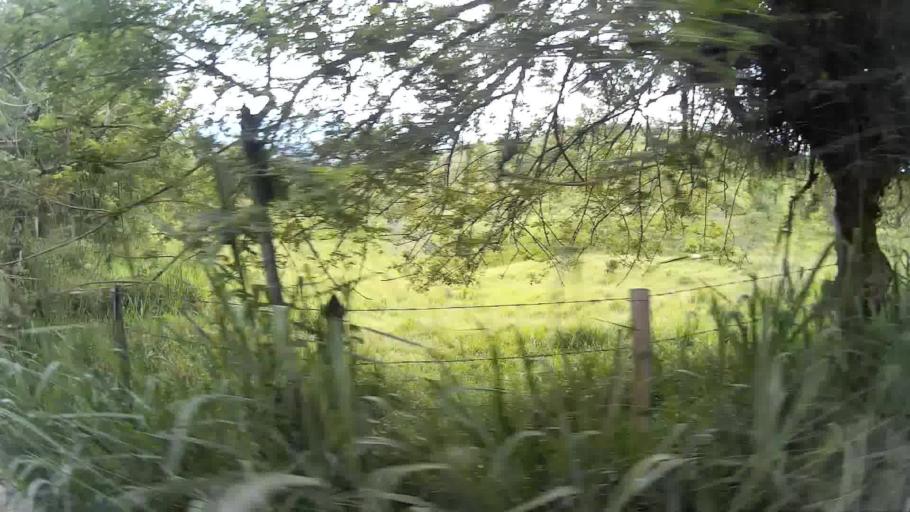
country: CO
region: Risaralda
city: La Virginia
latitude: 4.9334
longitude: -75.8533
